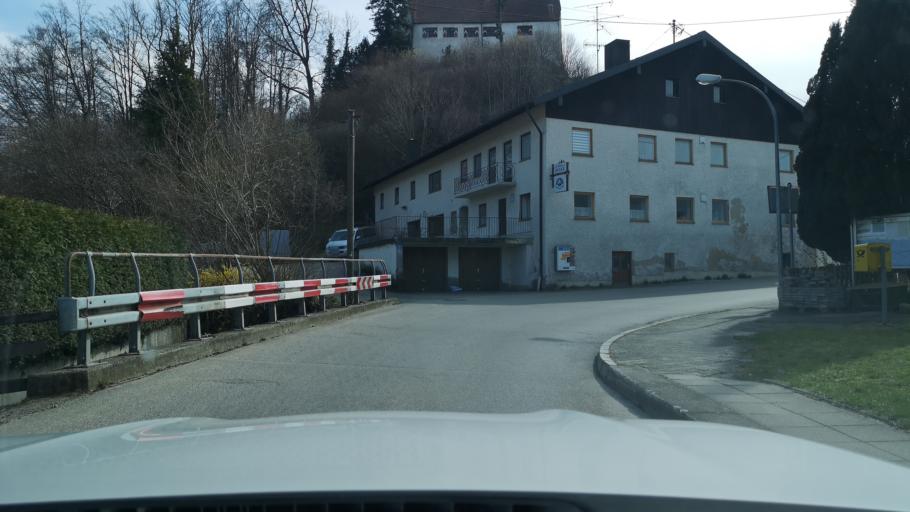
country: DE
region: Bavaria
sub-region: Upper Bavaria
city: Isen
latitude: 48.1893
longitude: 12.0491
